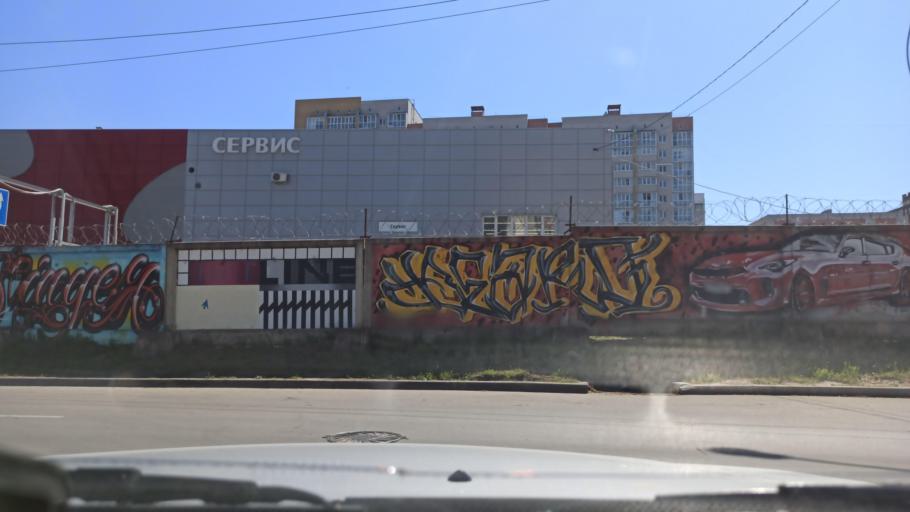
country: RU
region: Vologda
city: Vologda
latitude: 59.1934
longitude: 39.8293
